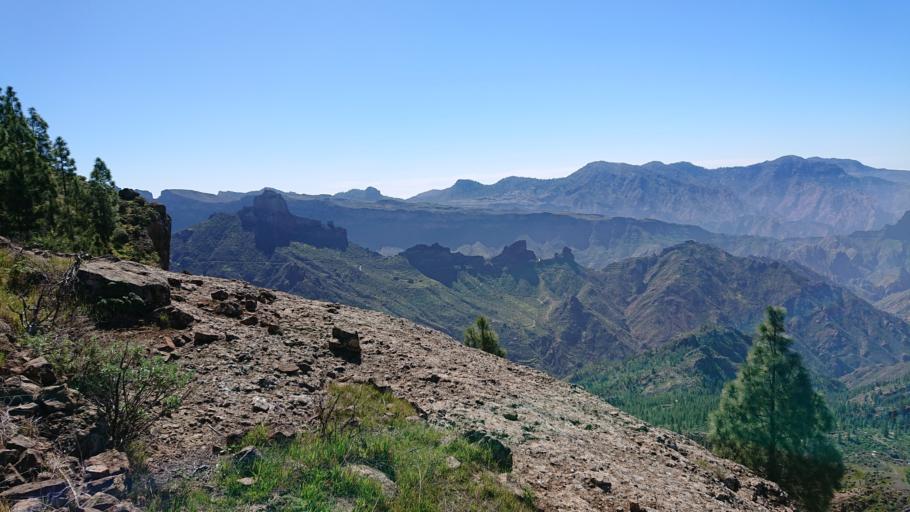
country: ES
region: Canary Islands
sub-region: Provincia de Las Palmas
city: Artenara
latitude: 28.0190
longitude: -15.6398
